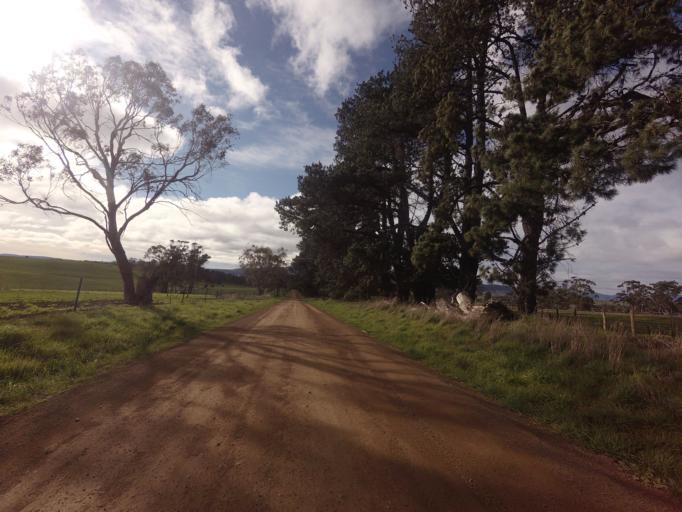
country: AU
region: Tasmania
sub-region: Derwent Valley
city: New Norfolk
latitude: -42.7162
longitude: 146.8815
